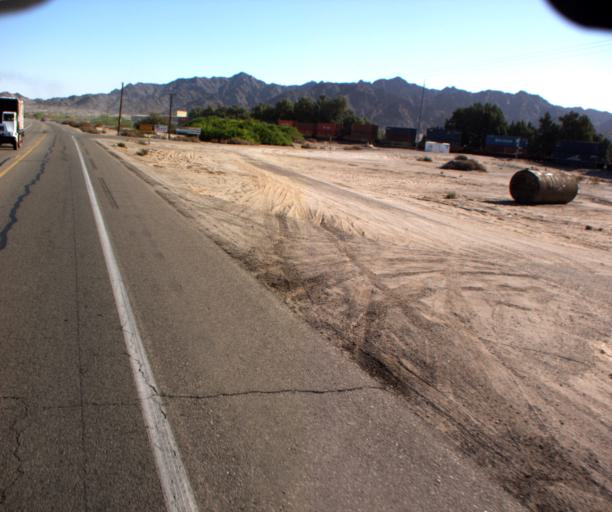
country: US
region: Arizona
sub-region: Yuma County
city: Fortuna Foothills
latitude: 32.7112
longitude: -114.4290
